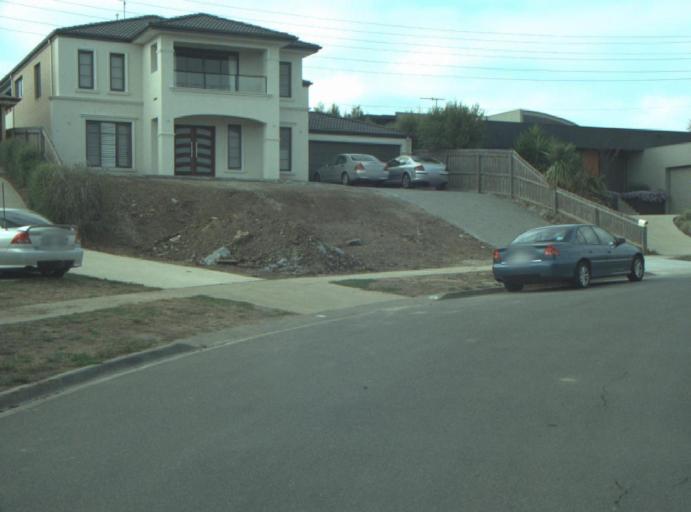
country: AU
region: Victoria
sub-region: Greater Geelong
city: Wandana Heights
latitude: -38.1548
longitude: 144.3142
